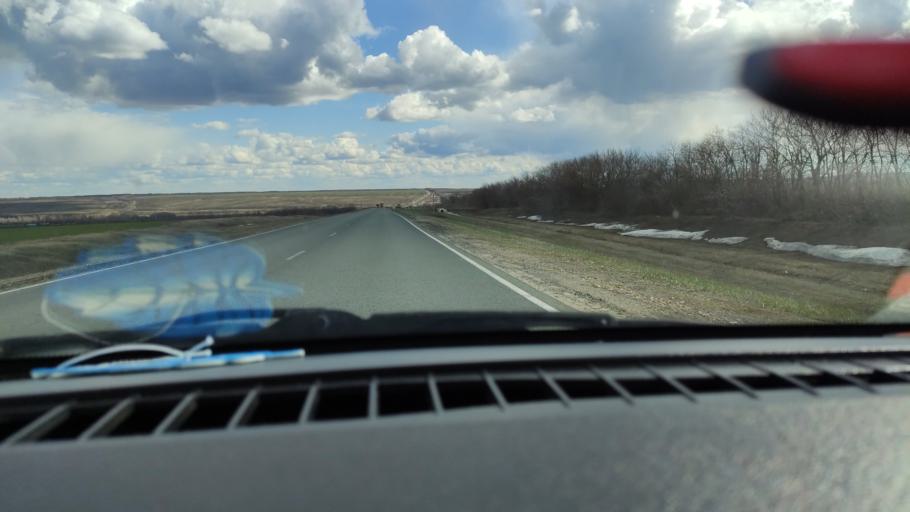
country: RU
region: Saratov
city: Dukhovnitskoye
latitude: 52.7564
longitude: 48.2445
